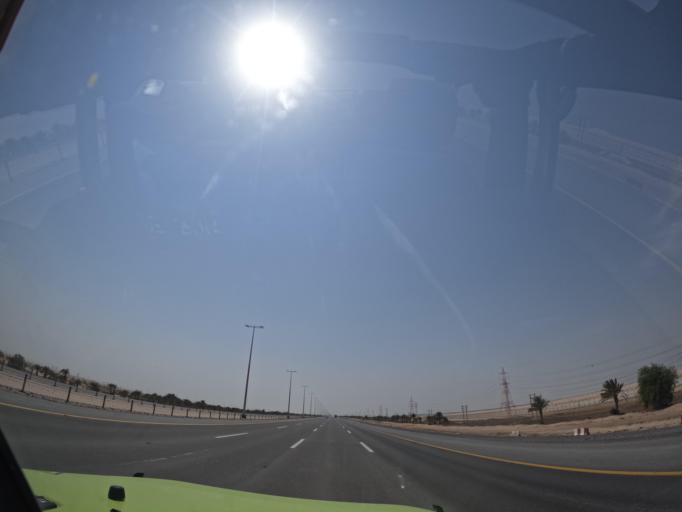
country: AE
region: Abu Dhabi
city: Abu Dhabi
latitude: 24.2029
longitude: 54.3998
